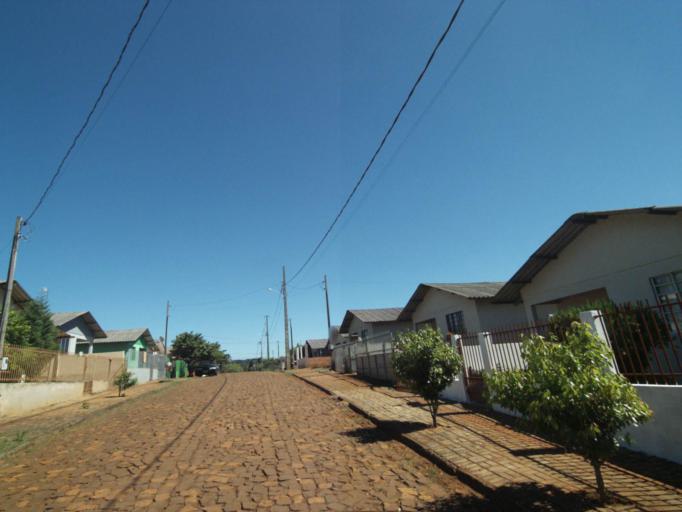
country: BR
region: Santa Catarina
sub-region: Sao Lourenco Do Oeste
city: Sao Lourenco dOeste
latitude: -26.2730
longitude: -52.7776
